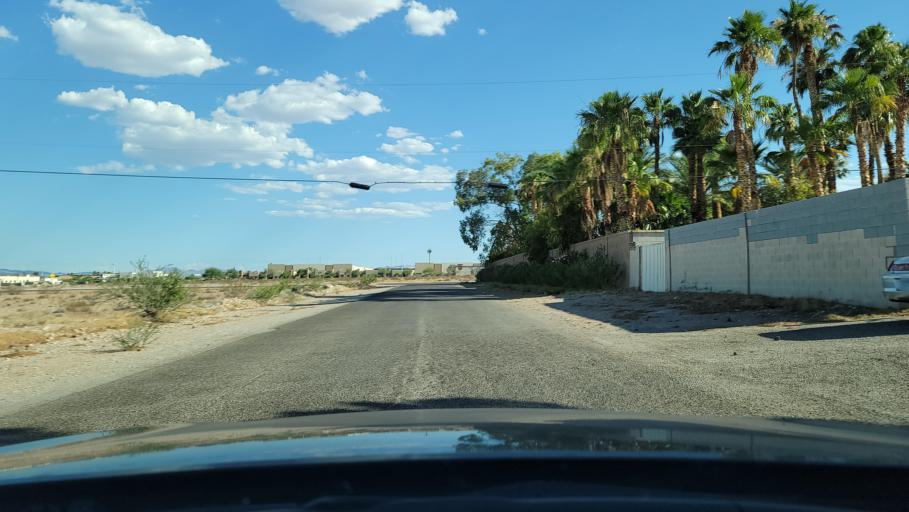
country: US
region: Nevada
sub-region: Clark County
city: Spring Valley
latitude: 36.0793
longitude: -115.2271
